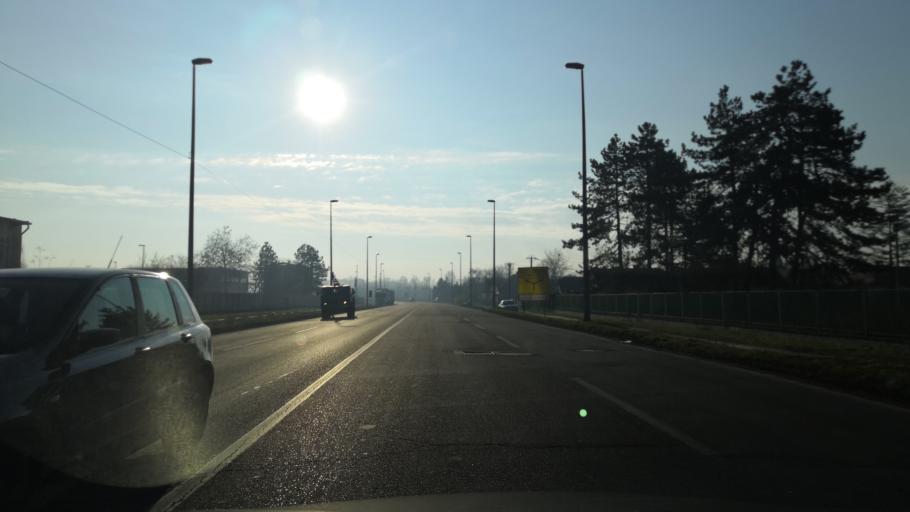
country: RS
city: Pocerski Pricinovic
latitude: 44.7431
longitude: 19.7213
